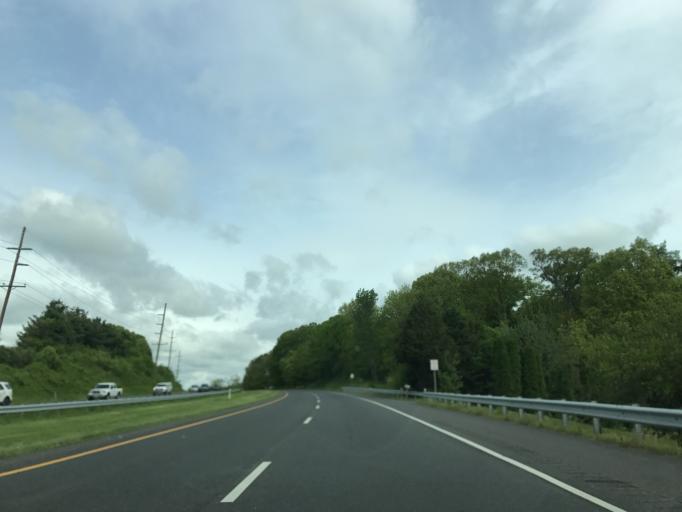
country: US
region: Maryland
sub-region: Carroll County
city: Westminster
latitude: 39.5208
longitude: -76.9148
